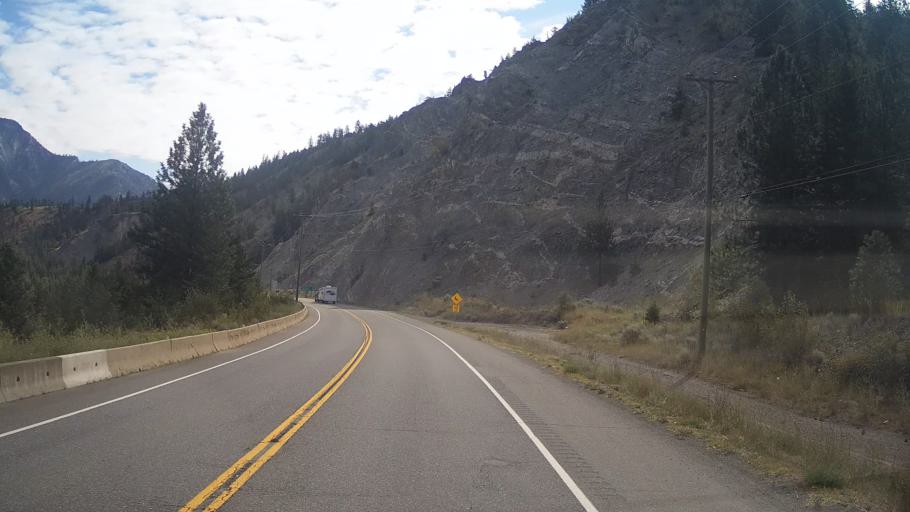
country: CA
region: British Columbia
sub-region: Thompson-Nicola Regional District
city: Ashcroft
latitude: 50.2495
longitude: -121.5579
